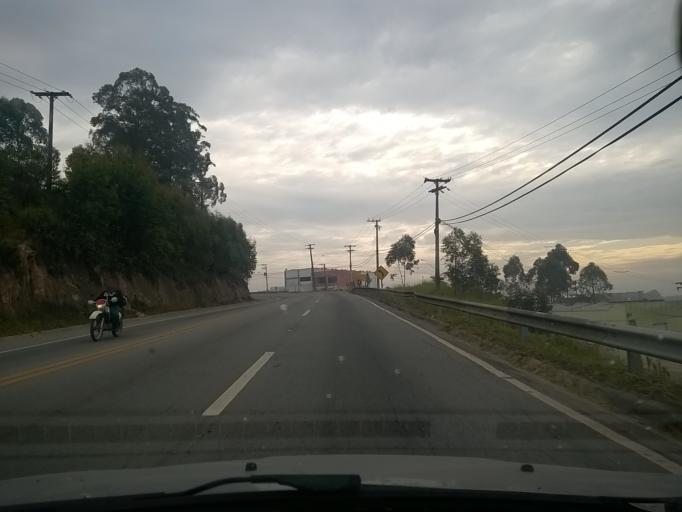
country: BR
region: Sao Paulo
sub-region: Francisco Morato
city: Francisco Morato
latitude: -23.3099
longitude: -46.7573
